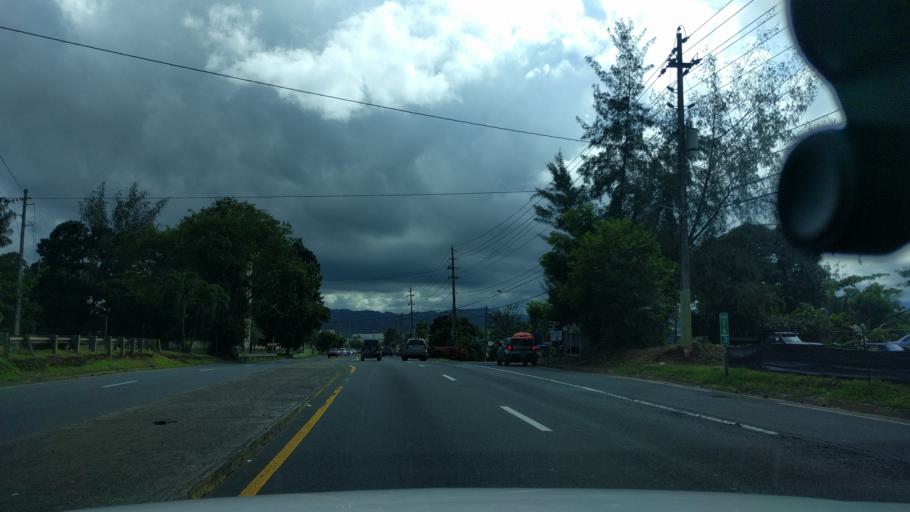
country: PR
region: Toa Alta
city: Pajaros
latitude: 18.3562
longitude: -66.1900
